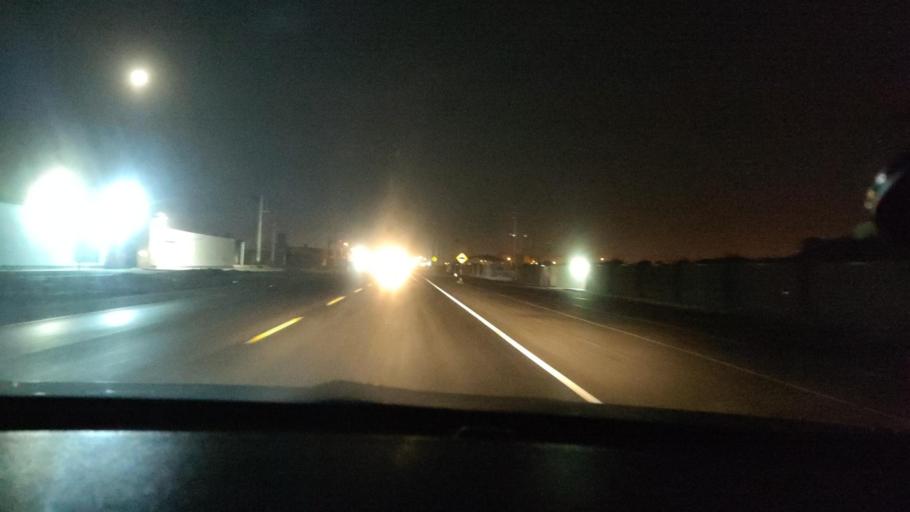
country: PE
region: La Libertad
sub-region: Provincia de Trujillo
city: Buenos Aires
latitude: -8.1524
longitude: -79.0387
